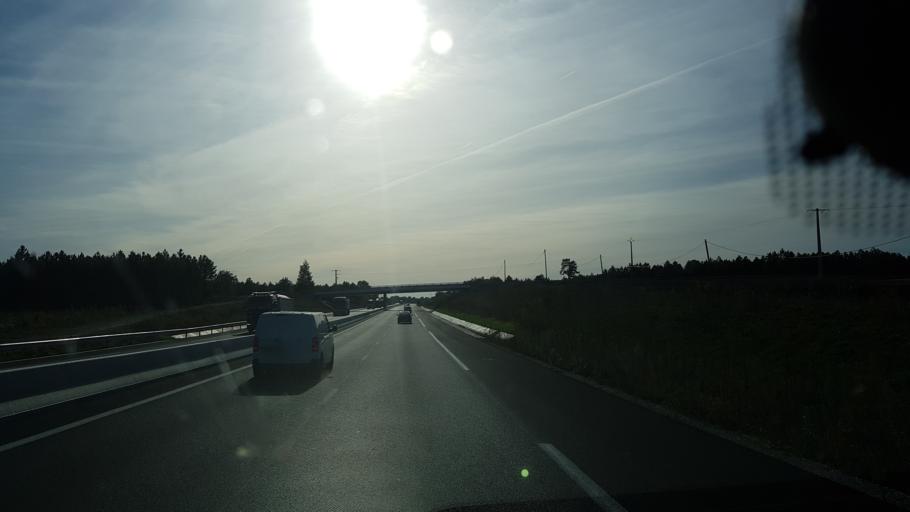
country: FR
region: Poitou-Charentes
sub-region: Departement de la Charente
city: Baignes-Sainte-Radegonde
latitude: 45.3466
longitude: -0.2062
